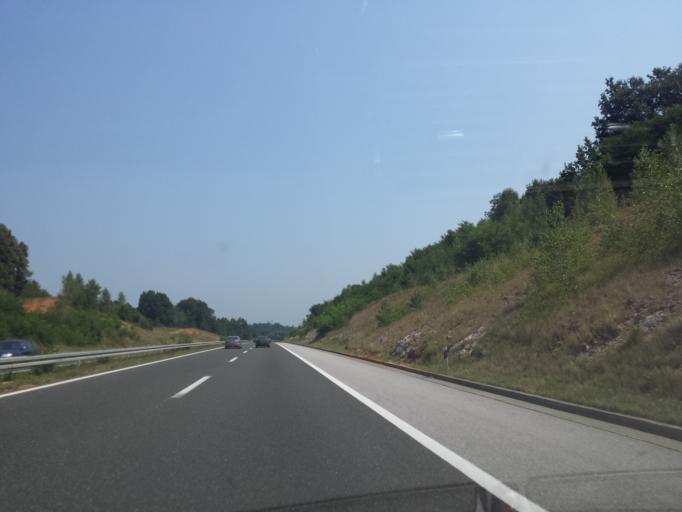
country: SI
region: Crnomelj
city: Crnomelj
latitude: 45.4362
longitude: 15.3296
